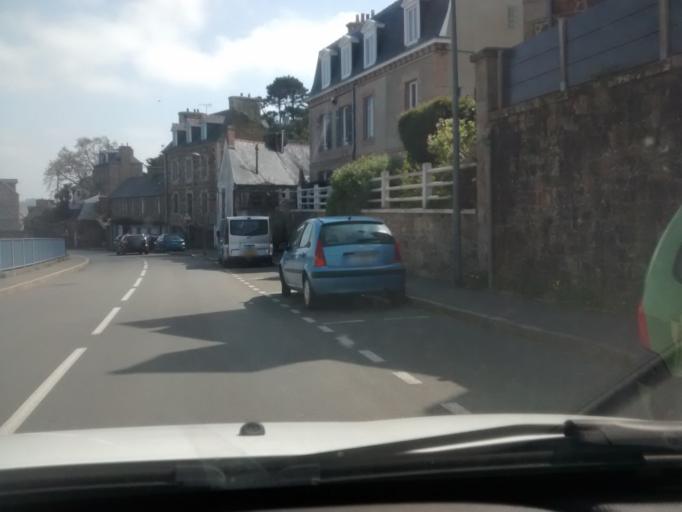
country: FR
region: Brittany
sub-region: Departement des Cotes-d'Armor
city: Perros-Guirec
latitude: 48.8134
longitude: -3.4419
